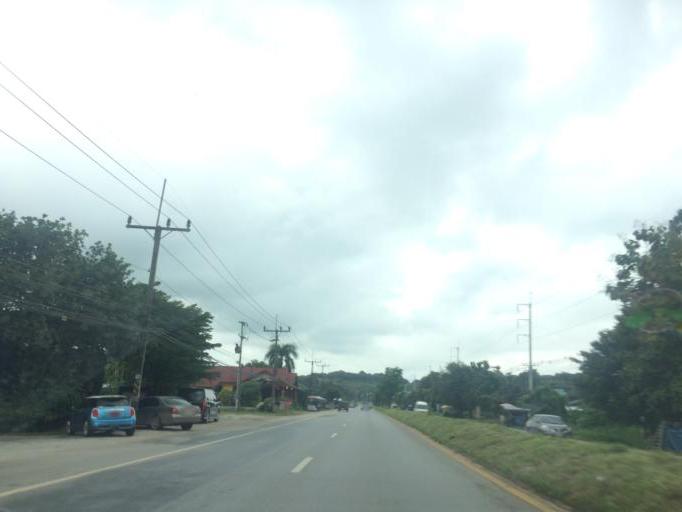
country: TH
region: Chiang Rai
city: Mae Chan
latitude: 20.1082
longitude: 99.8735
